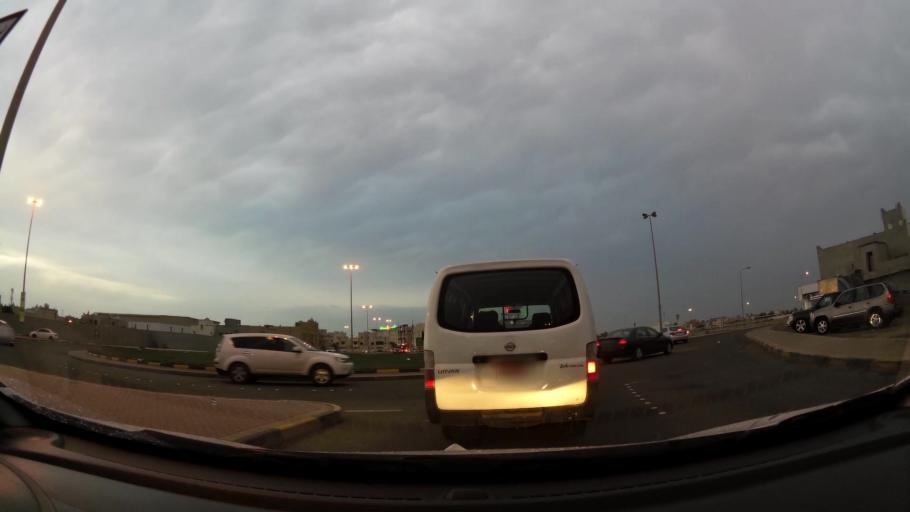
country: BH
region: Northern
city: Madinat `Isa
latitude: 26.1593
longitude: 50.5213
